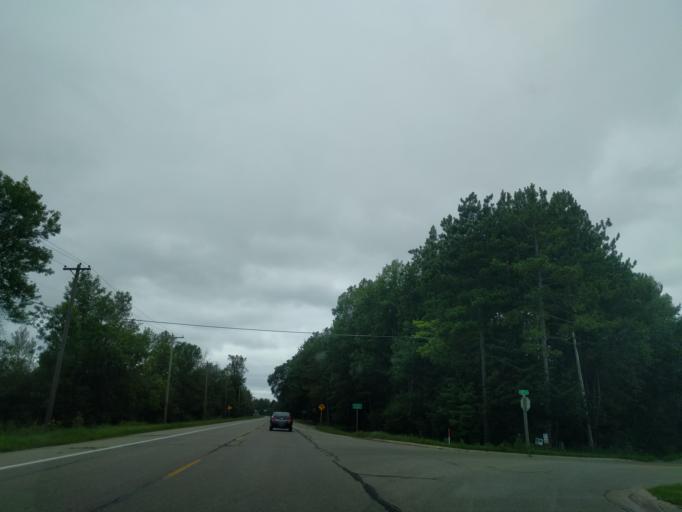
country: US
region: Michigan
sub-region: Delta County
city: Escanaba
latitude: 45.7102
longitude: -87.0956
